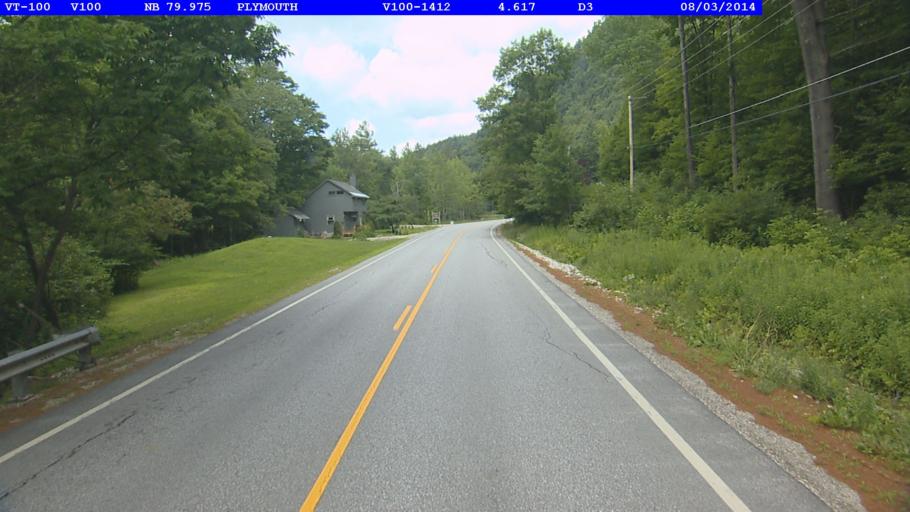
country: US
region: Vermont
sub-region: Windsor County
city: Woodstock
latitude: 43.5212
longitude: -72.7332
